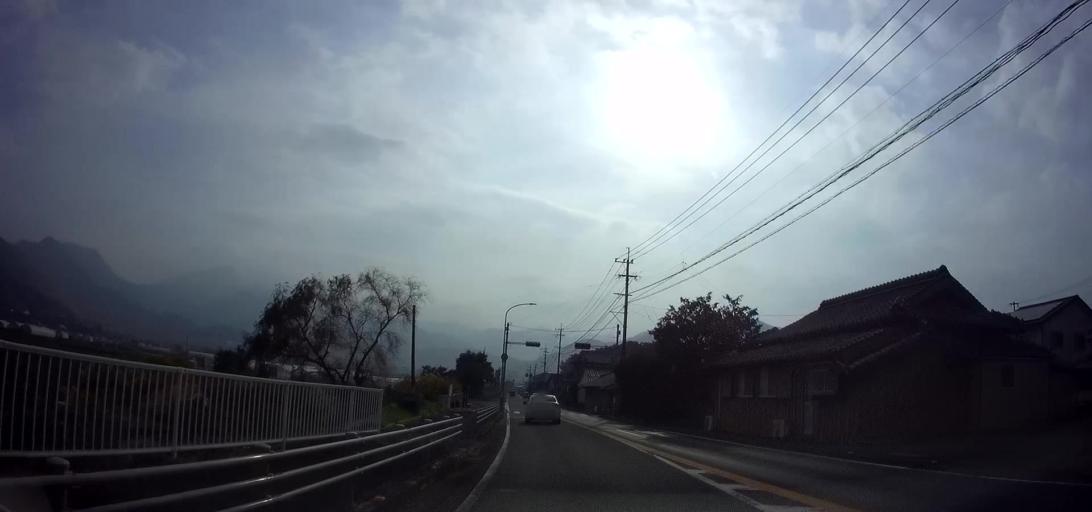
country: JP
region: Nagasaki
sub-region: Isahaya-shi
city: Isahaya
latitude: 32.7930
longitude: 130.1838
